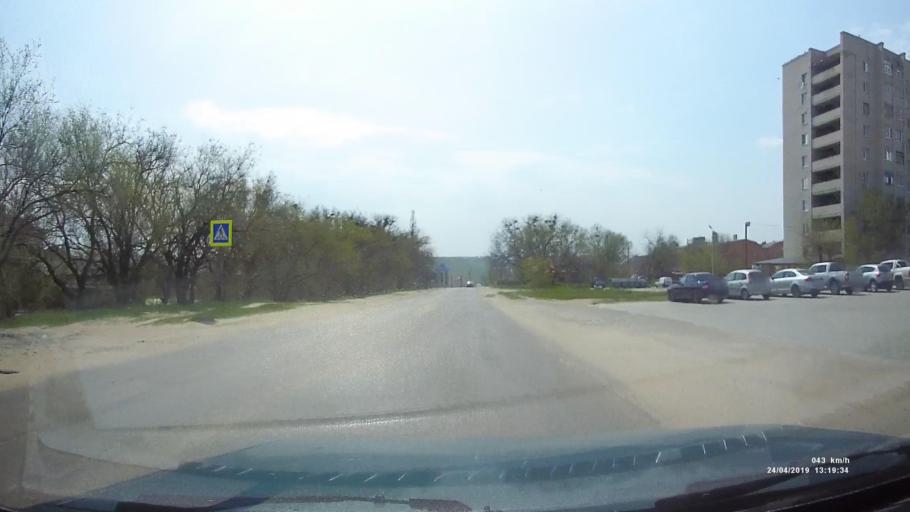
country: RU
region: Kalmykiya
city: Elista
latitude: 46.2994
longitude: 44.2900
